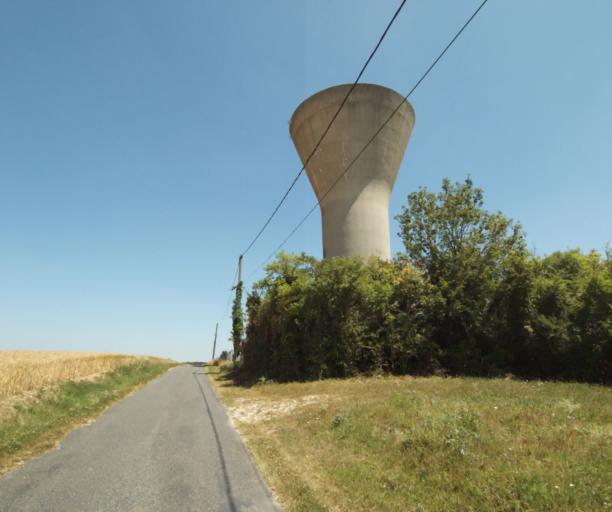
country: FR
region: Centre
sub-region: Departement du Loiret
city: Malesherbes
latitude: 48.3003
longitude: 2.4429
